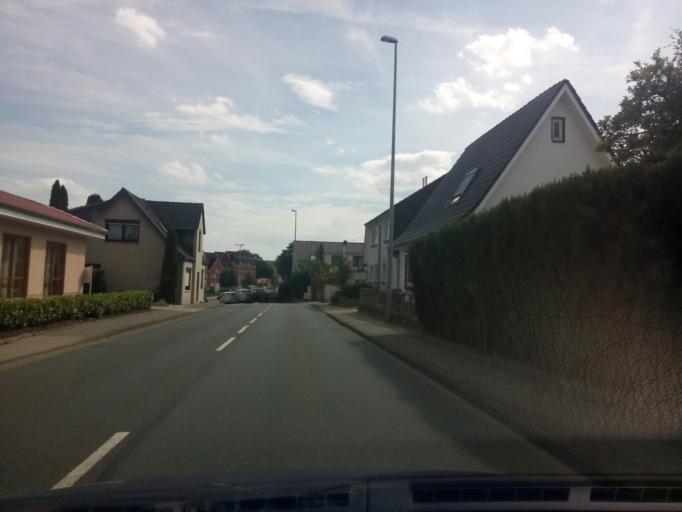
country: DE
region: Lower Saxony
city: Osterholz-Scharmbeck
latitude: 53.2269
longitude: 8.7974
